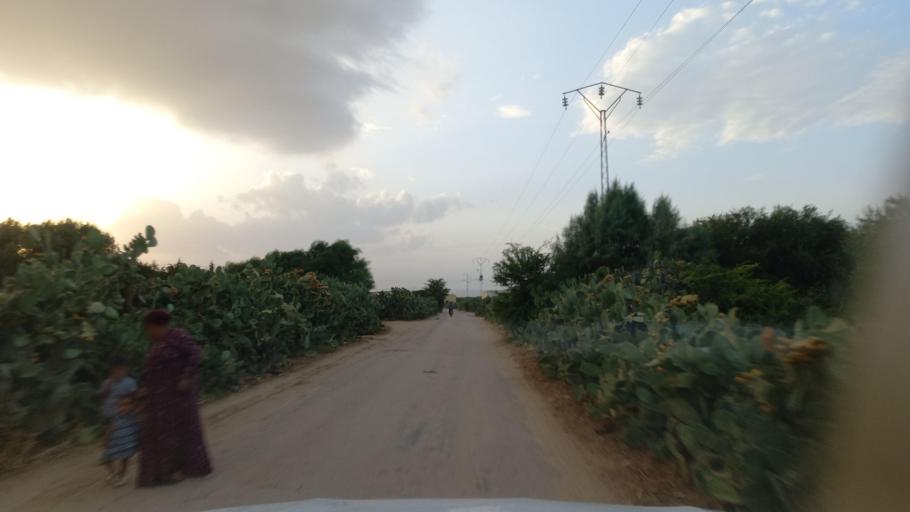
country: TN
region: Al Qasrayn
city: Kasserine
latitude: 35.2703
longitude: 9.0568
